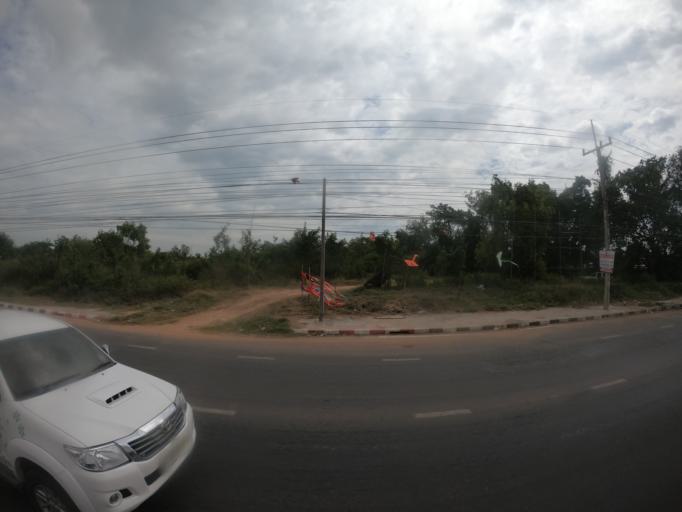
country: TH
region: Maha Sarakham
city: Maha Sarakham
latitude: 16.2445
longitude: 103.2725
